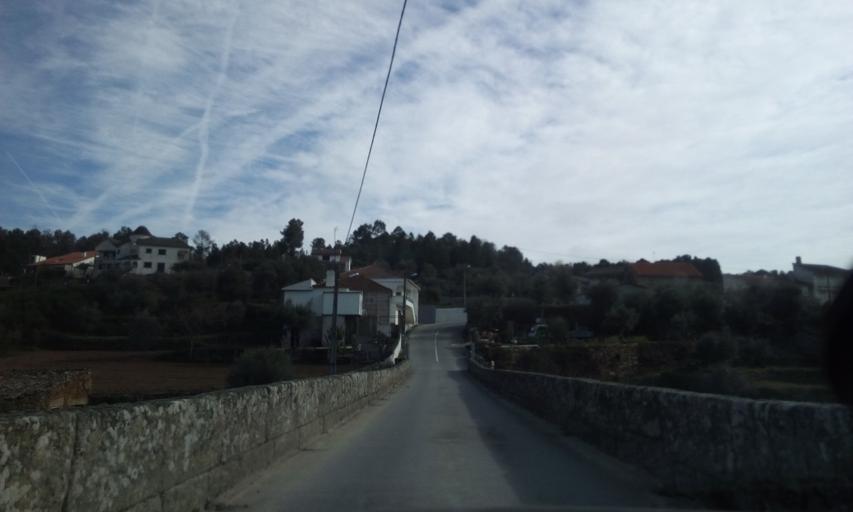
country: PT
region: Guarda
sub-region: Fornos de Algodres
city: Fornos de Algodres
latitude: 40.6828
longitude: -7.5324
